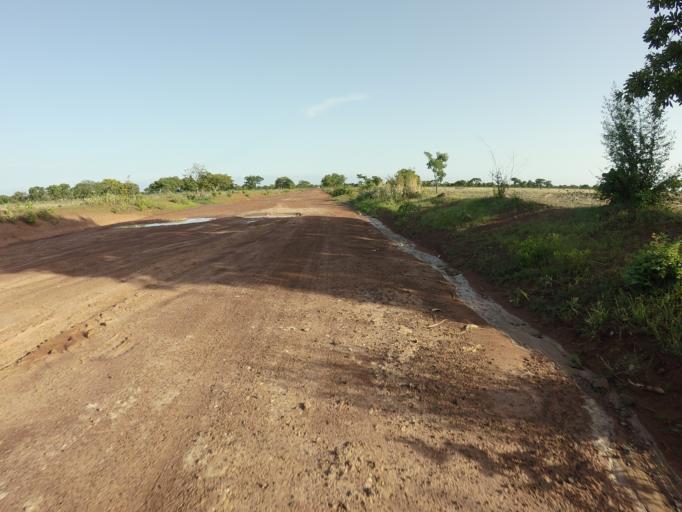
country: TG
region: Savanes
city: Sansanne-Mango
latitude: 10.3751
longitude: -0.0944
